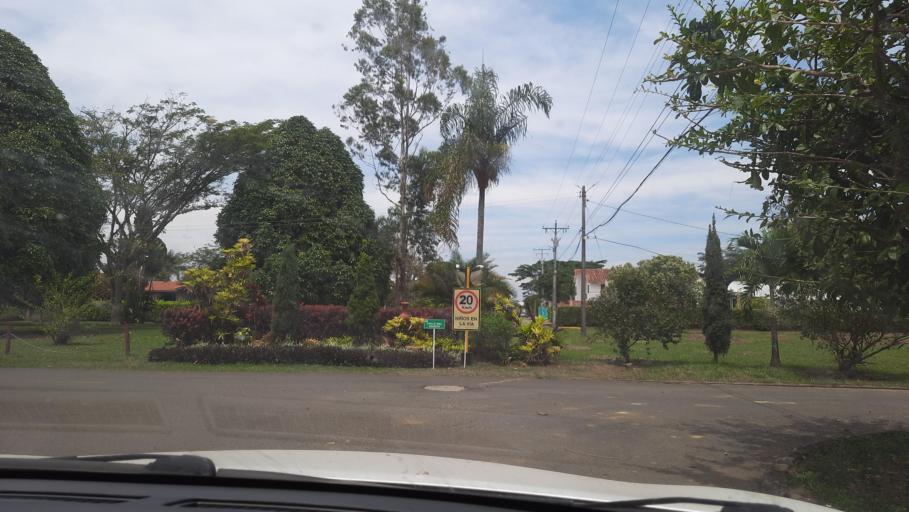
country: CO
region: Valle del Cauca
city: Jamundi
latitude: 3.2691
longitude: -76.5220
